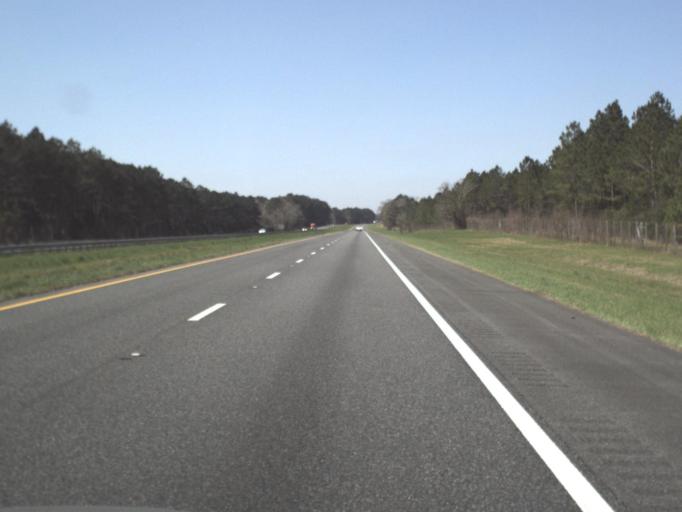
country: US
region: Florida
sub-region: Jackson County
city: Marianna
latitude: 30.7574
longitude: -85.3418
